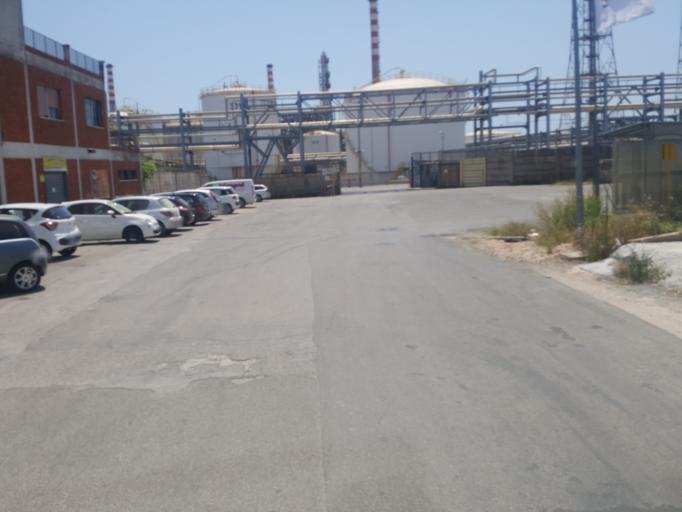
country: IT
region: Apulia
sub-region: Provincia di Taranto
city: Statte
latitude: 40.4967
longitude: 17.1968
